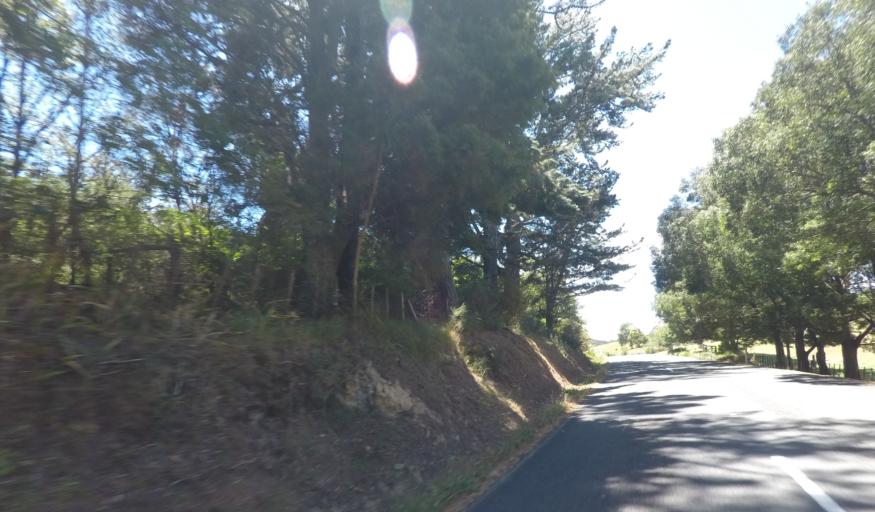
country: NZ
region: Northland
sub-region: Whangarei
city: Whangarei
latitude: -35.5452
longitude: 174.3060
